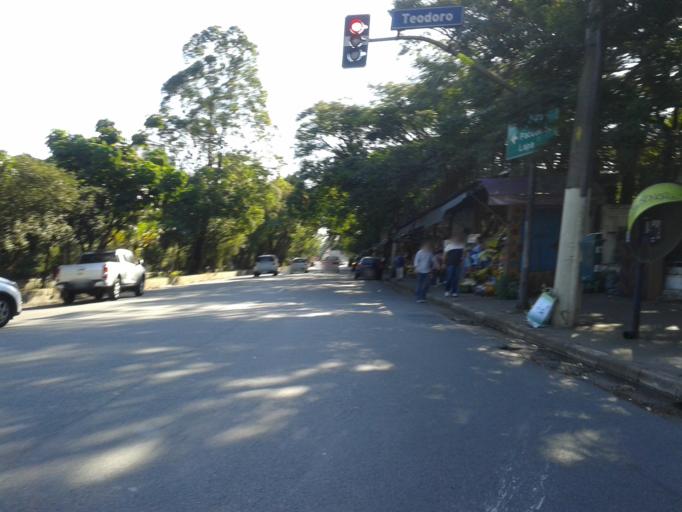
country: BR
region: Sao Paulo
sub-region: Sao Paulo
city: Sao Paulo
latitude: -23.5537
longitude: -46.6716
